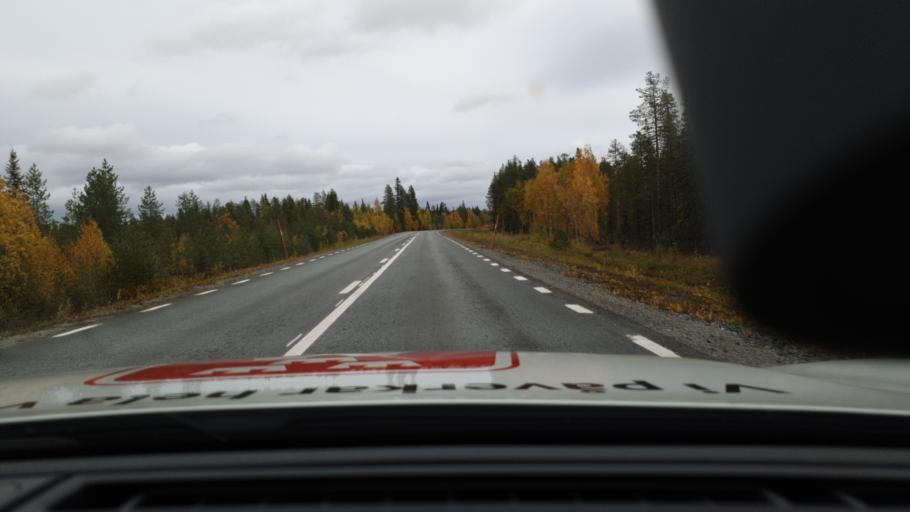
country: SE
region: Vaesterbotten
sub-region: Sorsele Kommun
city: Sorsele
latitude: 65.5372
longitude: 17.5904
